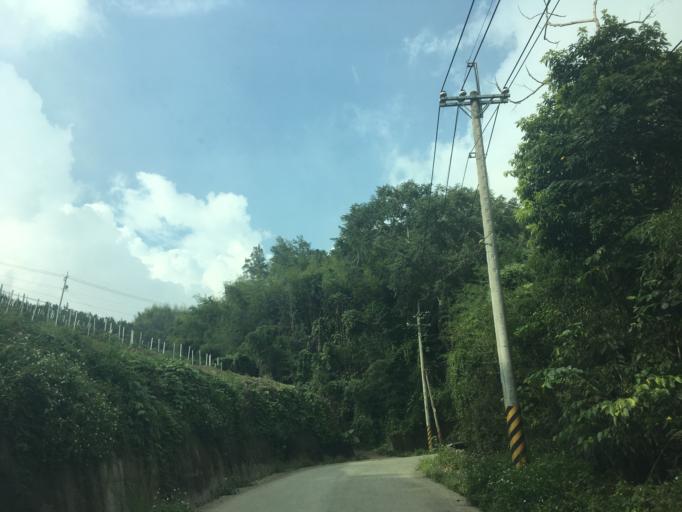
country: TW
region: Taiwan
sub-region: Miaoli
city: Miaoli
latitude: 24.4021
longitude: 120.9768
